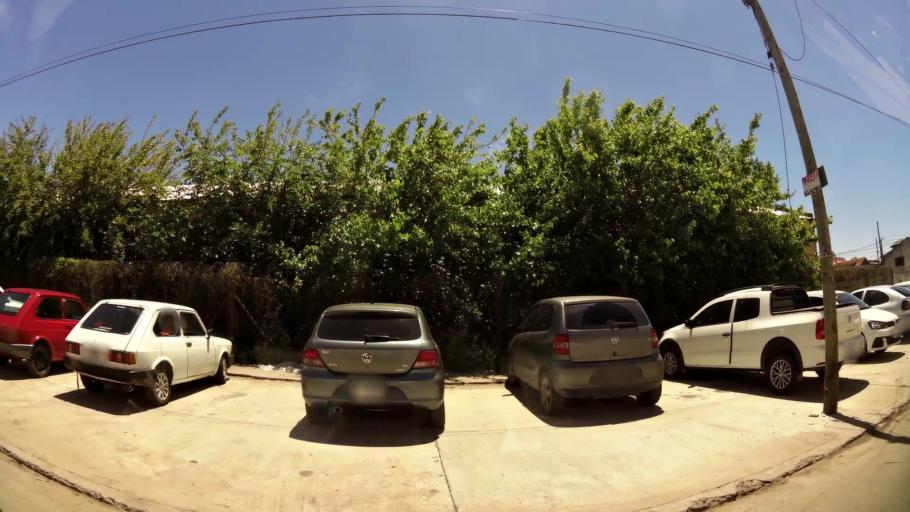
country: AR
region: Buenos Aires
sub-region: Partido de Quilmes
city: Quilmes
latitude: -34.7363
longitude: -58.2938
